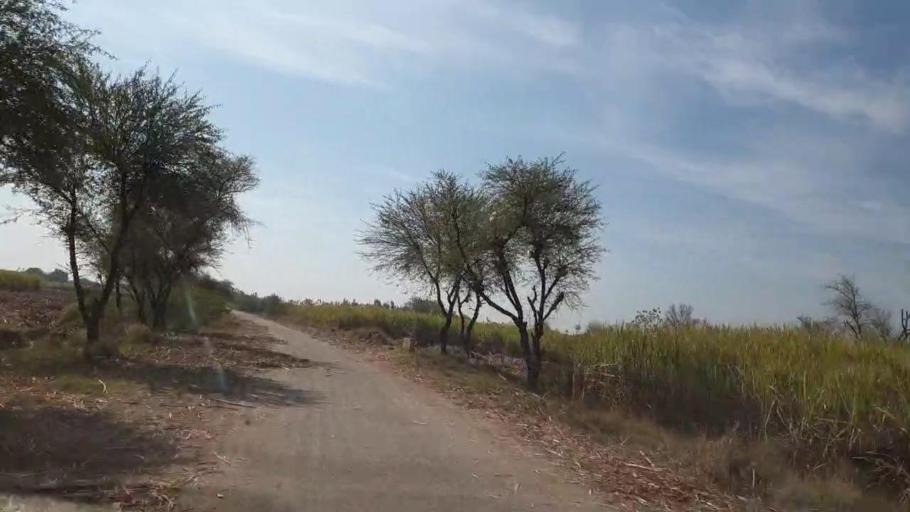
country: PK
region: Sindh
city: Mirpur Khas
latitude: 25.5269
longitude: 69.1451
